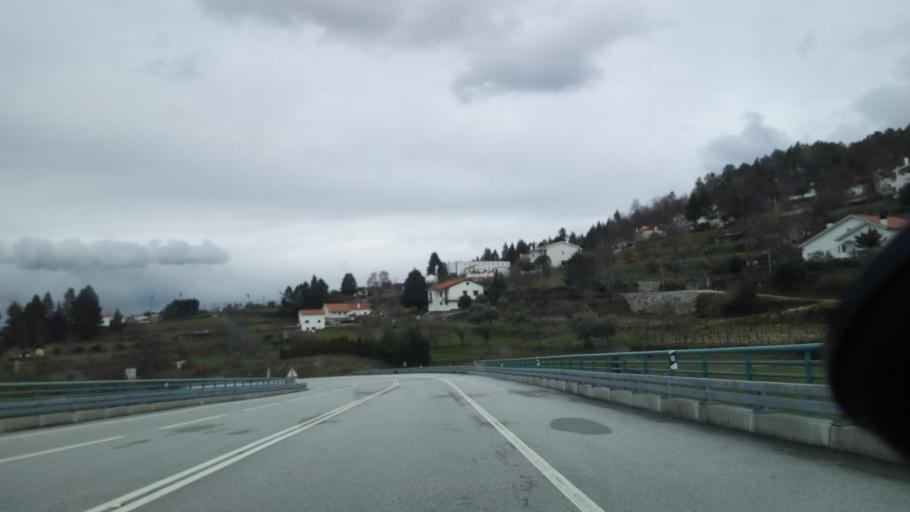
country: PT
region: Guarda
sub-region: Manteigas
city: Manteigas
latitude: 40.4802
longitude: -7.5974
